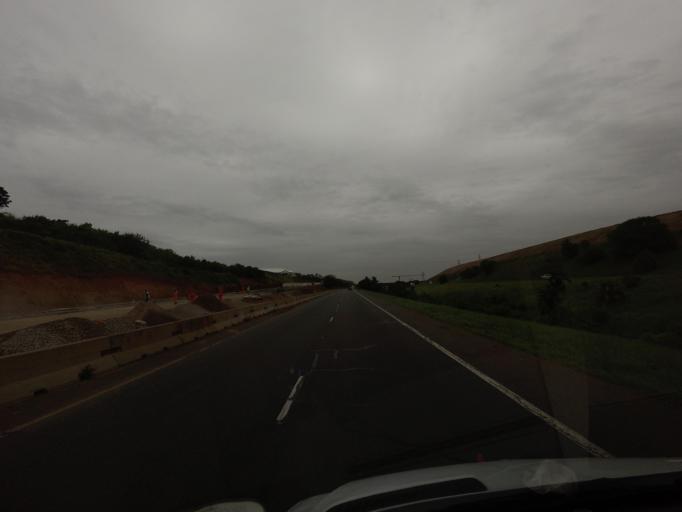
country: ZA
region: KwaZulu-Natal
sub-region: eThekwini Metropolitan Municipality
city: Durban
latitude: -29.7083
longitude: 31.0674
